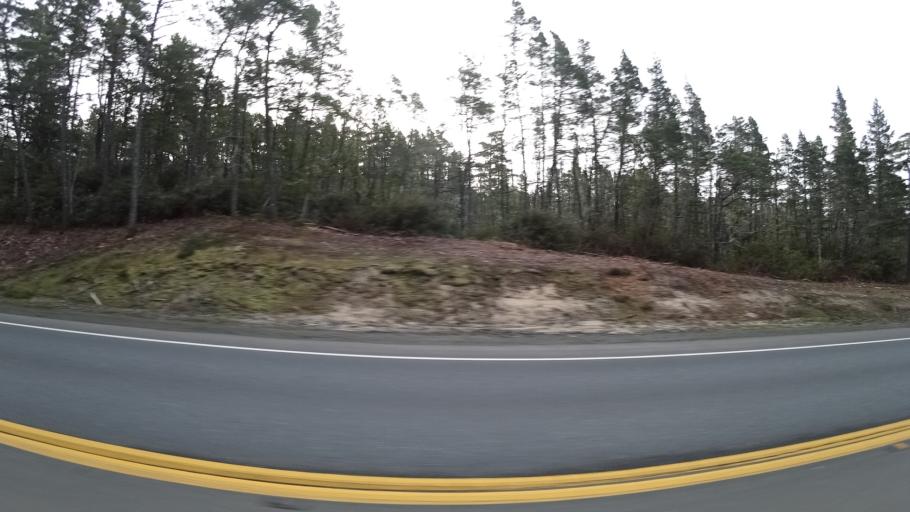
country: US
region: Oregon
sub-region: Coos County
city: Lakeside
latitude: 43.5853
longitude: -124.1845
